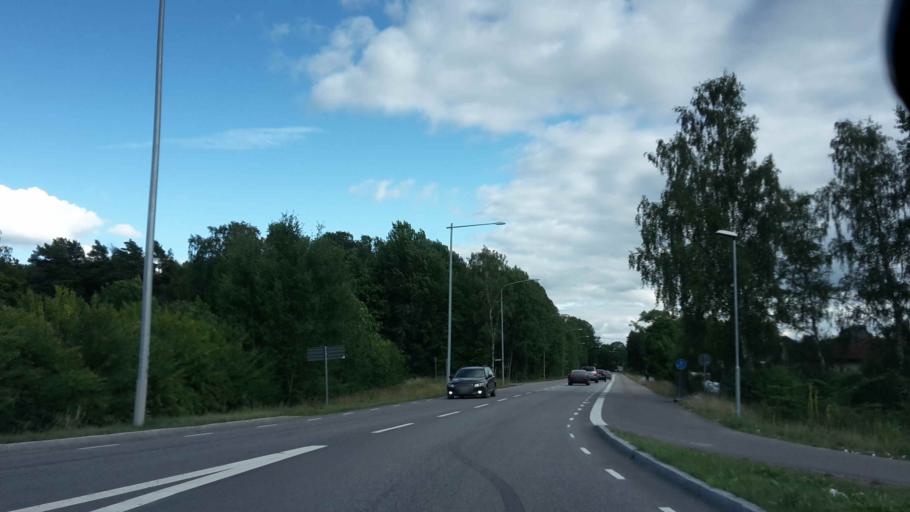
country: SE
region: OEstergoetland
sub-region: Norrkopings Kommun
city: Norrkoping
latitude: 58.6180
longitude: 16.1250
